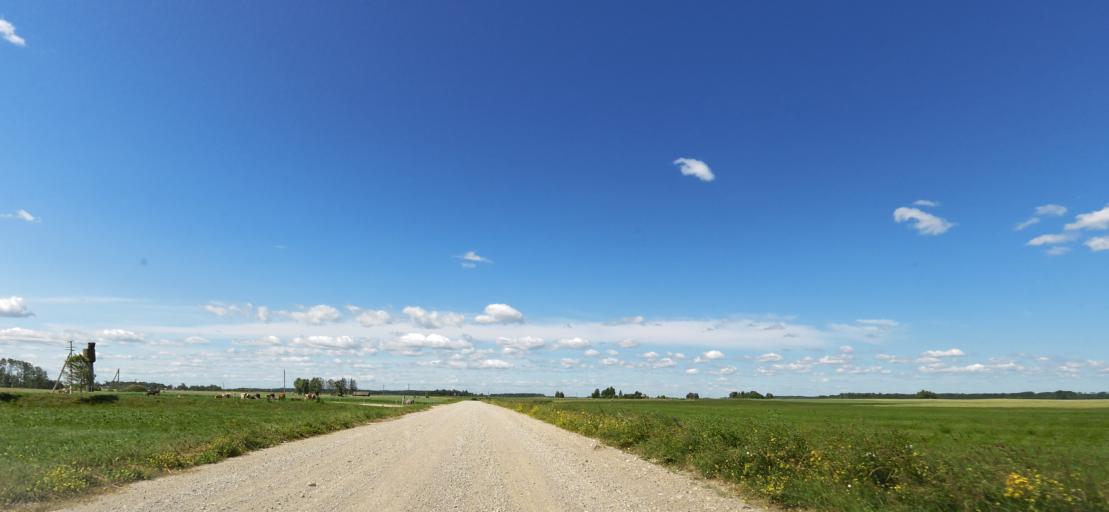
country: LT
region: Panevezys
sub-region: Birzai
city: Birzai
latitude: 56.2657
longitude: 24.5673
